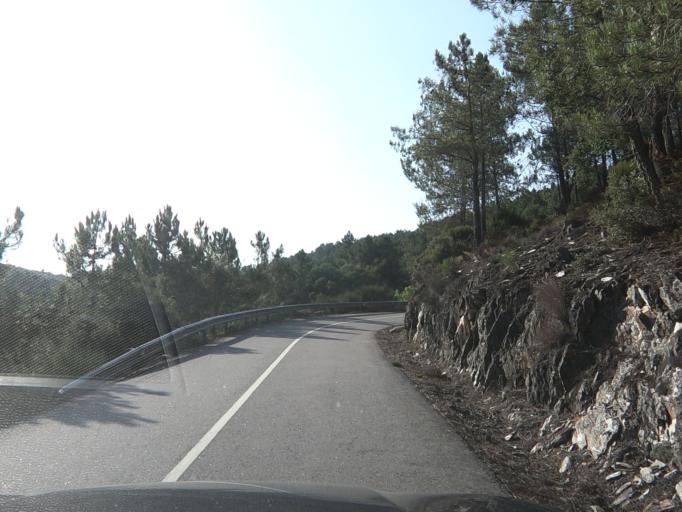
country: PT
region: Vila Real
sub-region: Sabrosa
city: Vilela
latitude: 41.2195
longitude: -7.6237
